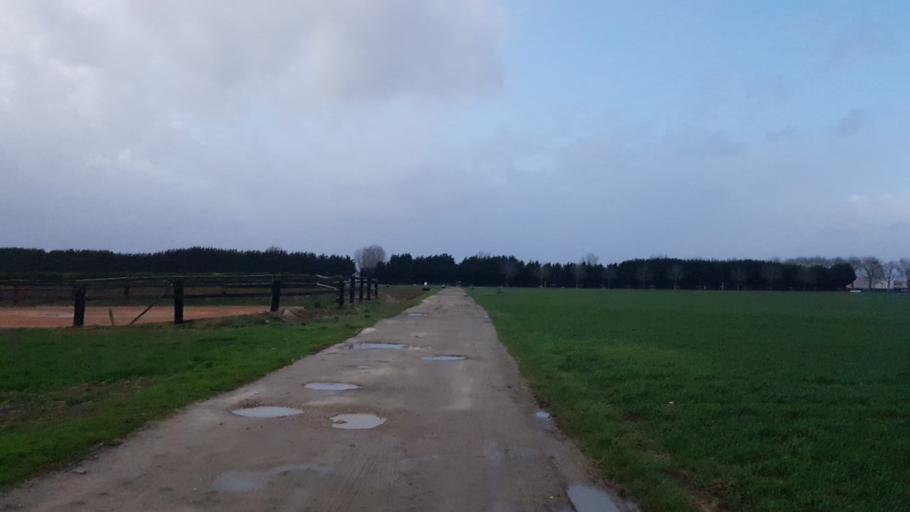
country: FR
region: Ile-de-France
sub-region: Departement de l'Essonne
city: Cheptainville
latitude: 48.5639
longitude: 2.2771
